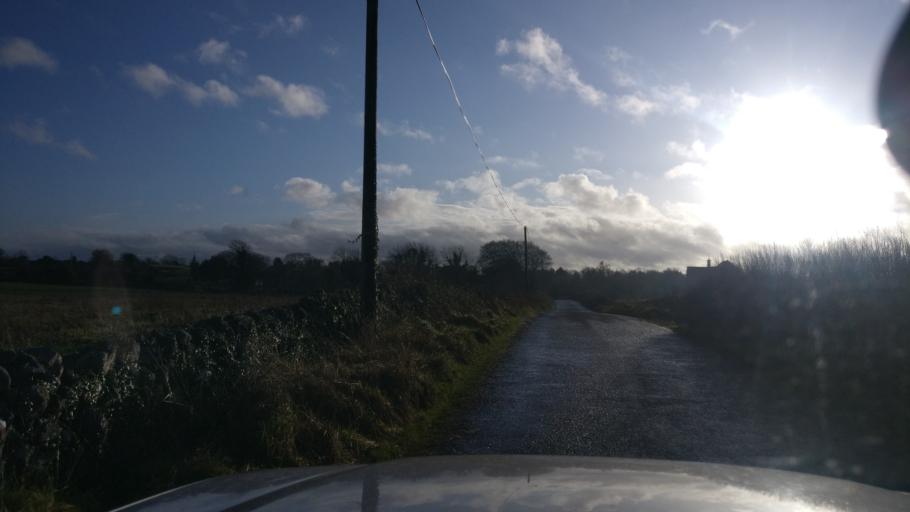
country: IE
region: Connaught
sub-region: County Galway
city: Loughrea
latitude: 53.2242
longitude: -8.5392
